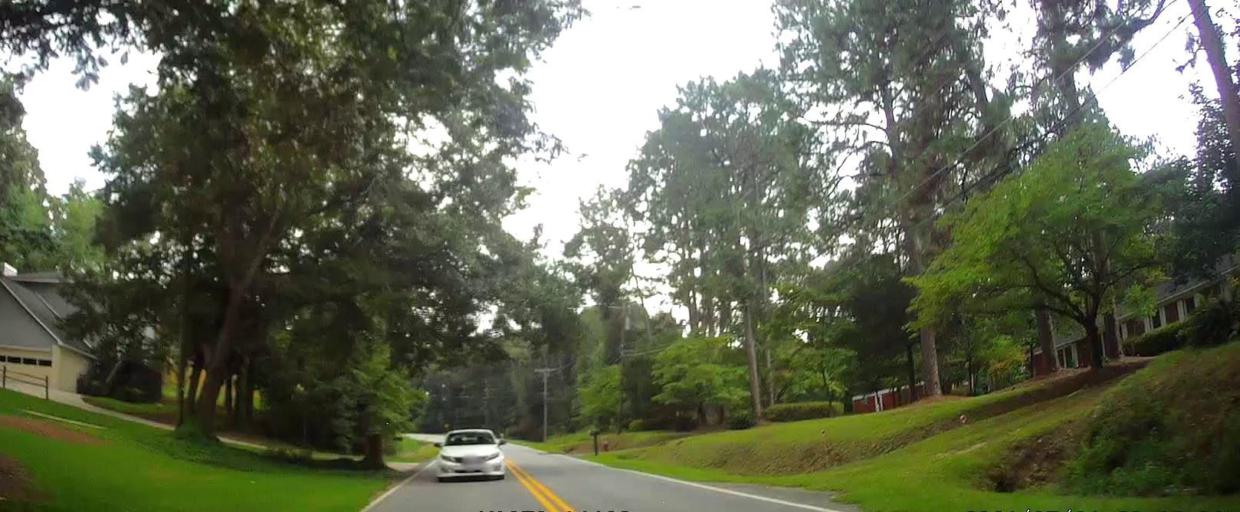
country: US
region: Georgia
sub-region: Houston County
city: Robins Air Force Base
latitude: 32.5708
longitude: -83.6090
